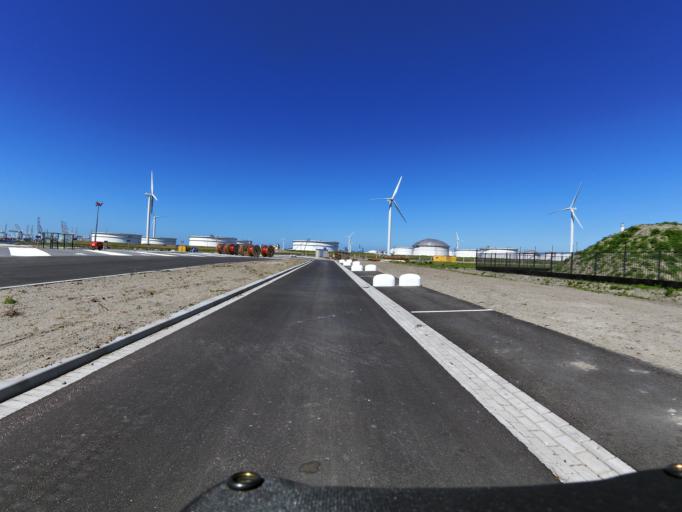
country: NL
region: South Holland
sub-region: Gemeente Rotterdam
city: Hoek van Holland
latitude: 51.9369
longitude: 4.0894
